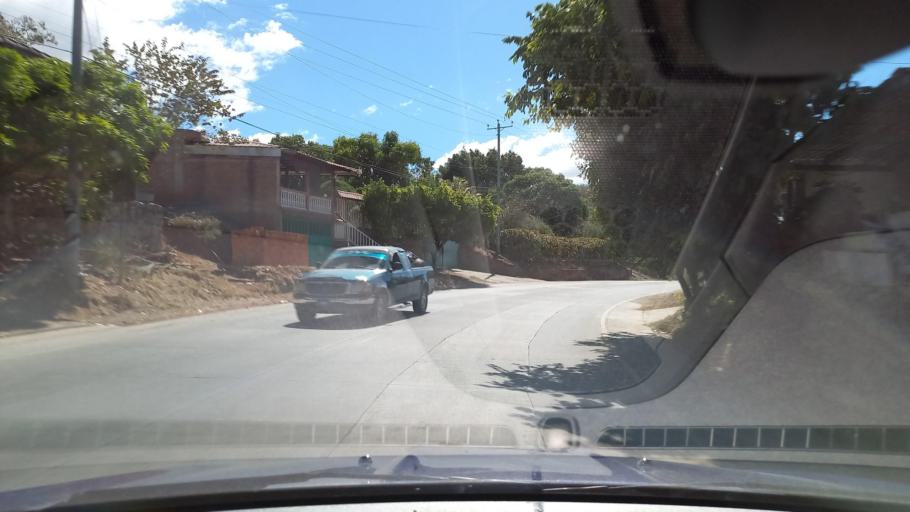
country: SV
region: Santa Ana
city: Metapan
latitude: 14.3511
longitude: -89.4530
